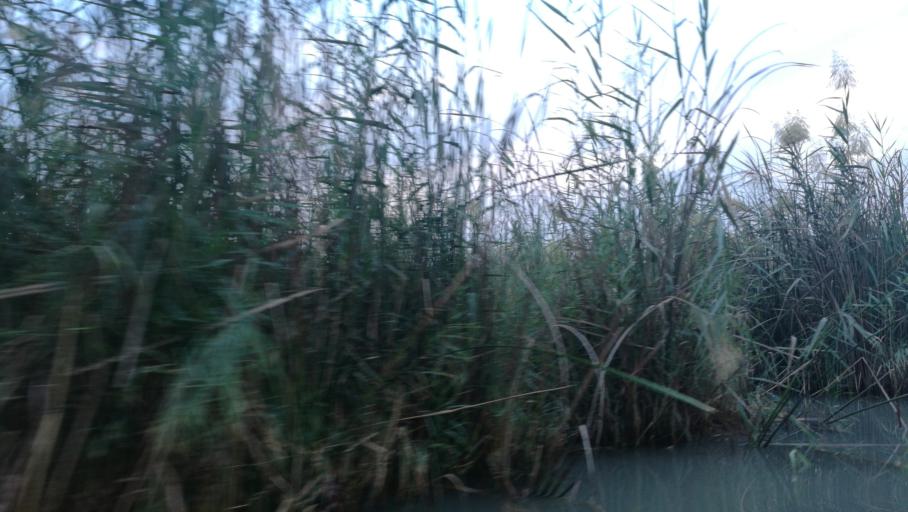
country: IQ
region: Dhi Qar
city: Al Jabayish
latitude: 30.9866
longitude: 47.0421
